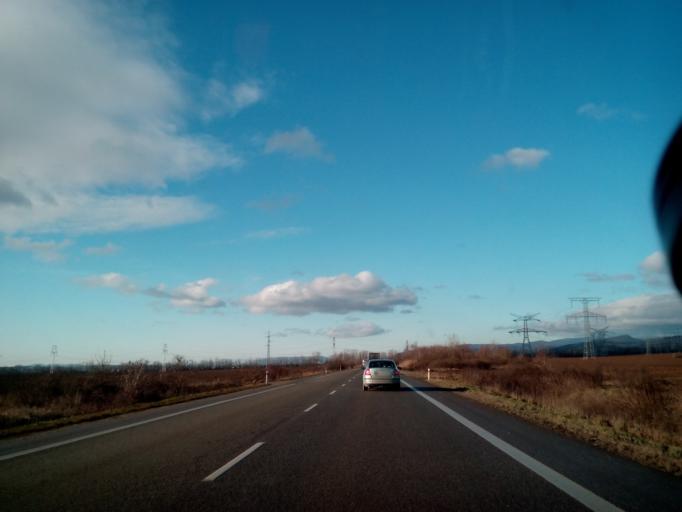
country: SK
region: Kosicky
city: Moldava nad Bodvou
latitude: 48.5979
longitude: 21.0555
